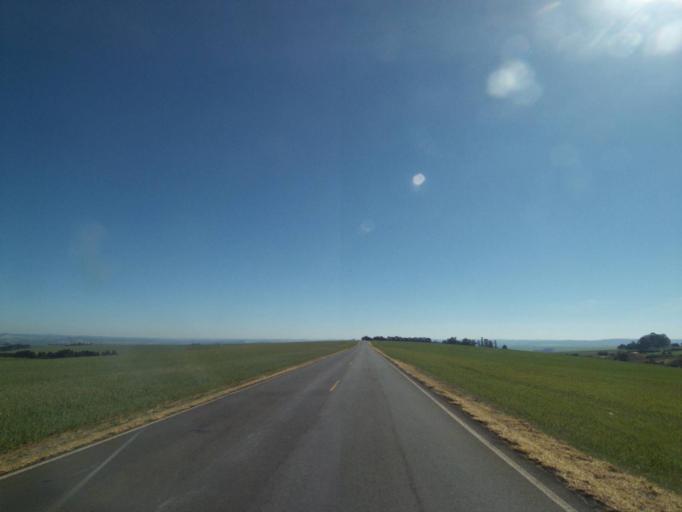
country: BR
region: Parana
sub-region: Tibagi
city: Tibagi
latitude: -24.5309
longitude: -50.3191
